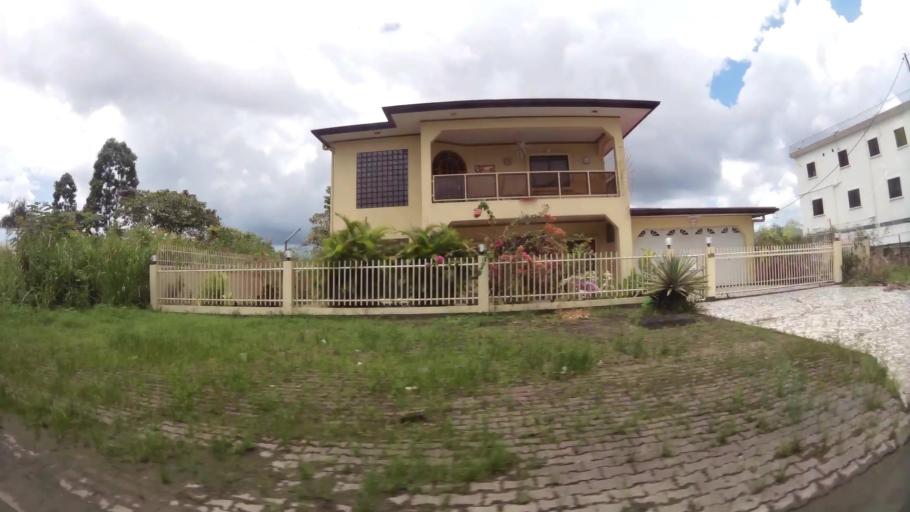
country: SR
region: Paramaribo
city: Paramaribo
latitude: 5.8576
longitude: -55.1349
